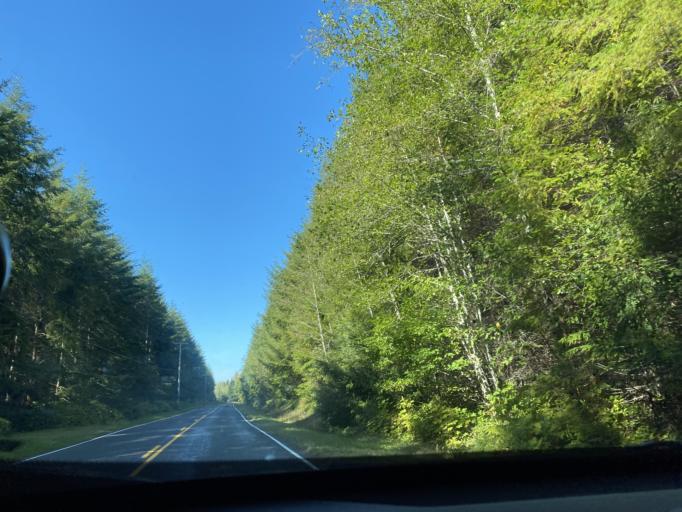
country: US
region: Washington
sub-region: Clallam County
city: Forks
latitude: 47.9470
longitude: -124.4927
